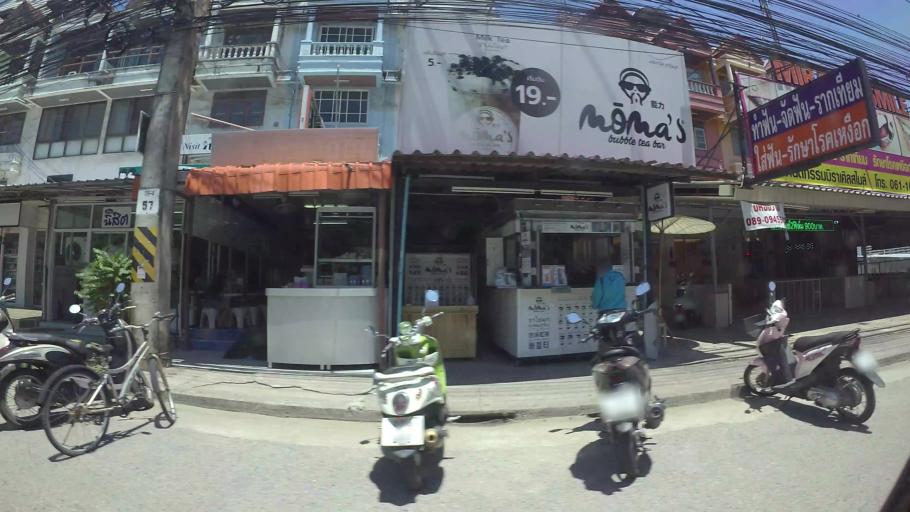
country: TH
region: Chon Buri
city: Si Racha
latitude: 13.1144
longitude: 100.9243
